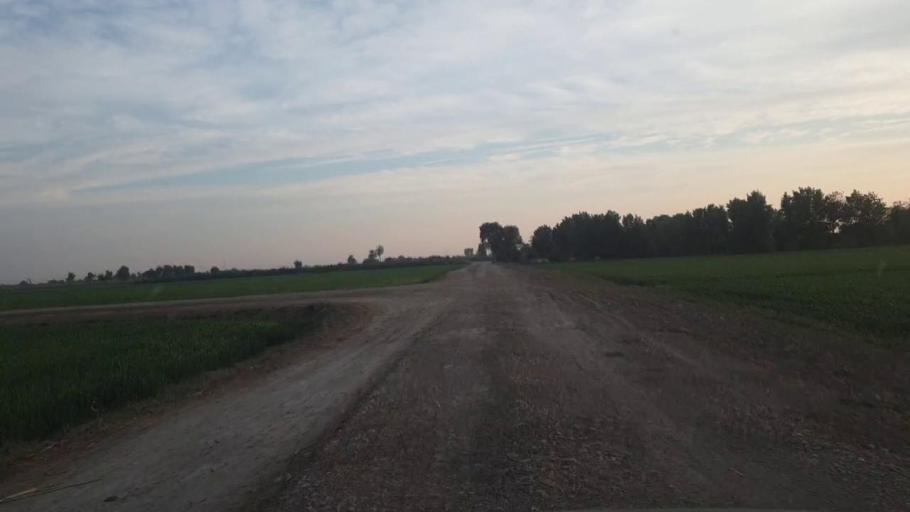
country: PK
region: Sindh
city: Shahdadpur
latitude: 26.0533
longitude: 68.5323
